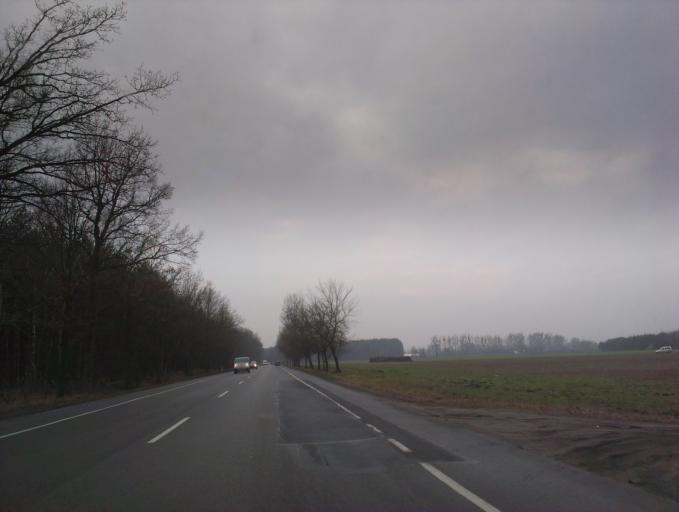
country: PL
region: Greater Poland Voivodeship
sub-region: Powiat obornicki
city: Rogozno
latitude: 52.7099
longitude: 16.9019
